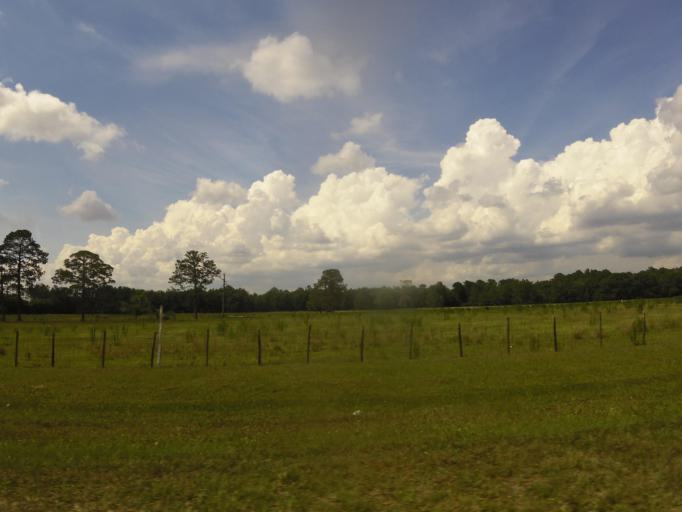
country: US
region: Florida
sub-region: Baker County
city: Macclenny
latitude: 30.2012
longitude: -82.0472
